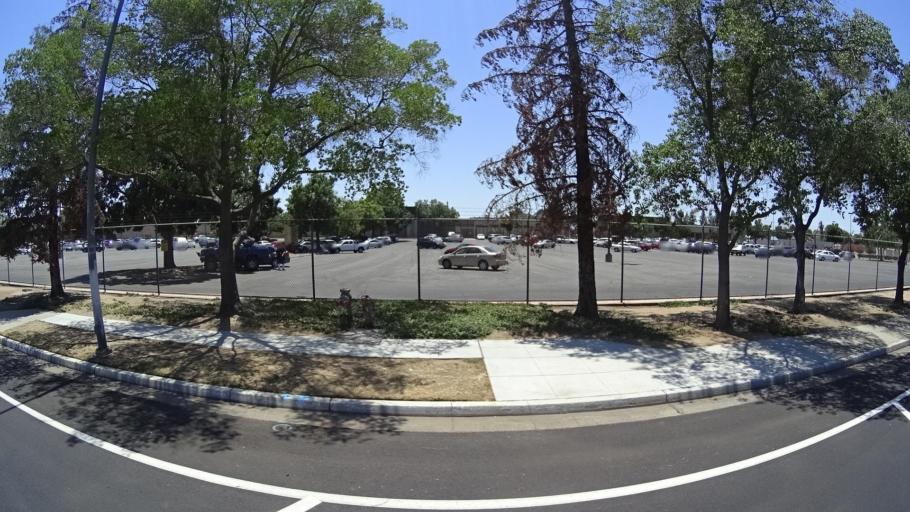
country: US
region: California
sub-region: Fresno County
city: Sunnyside
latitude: 36.7323
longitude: -119.7255
